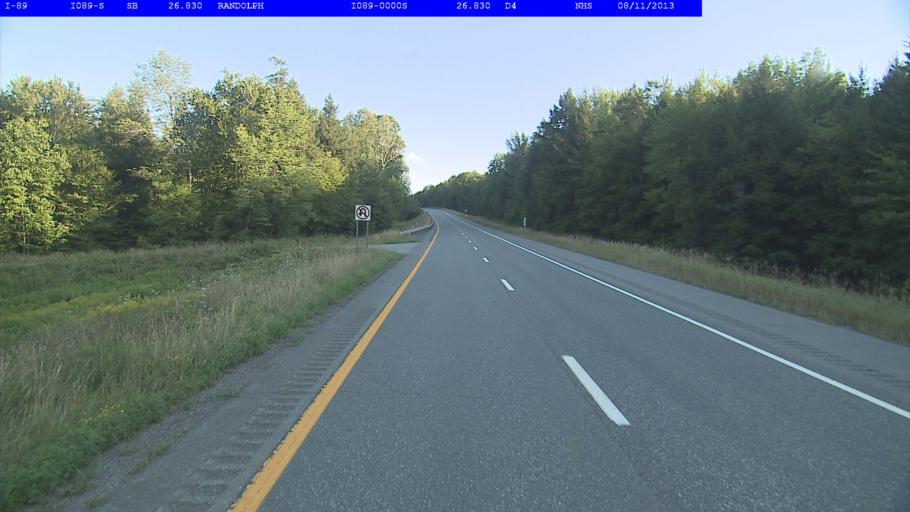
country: US
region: Vermont
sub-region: Orange County
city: Randolph
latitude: 43.8872
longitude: -72.6178
